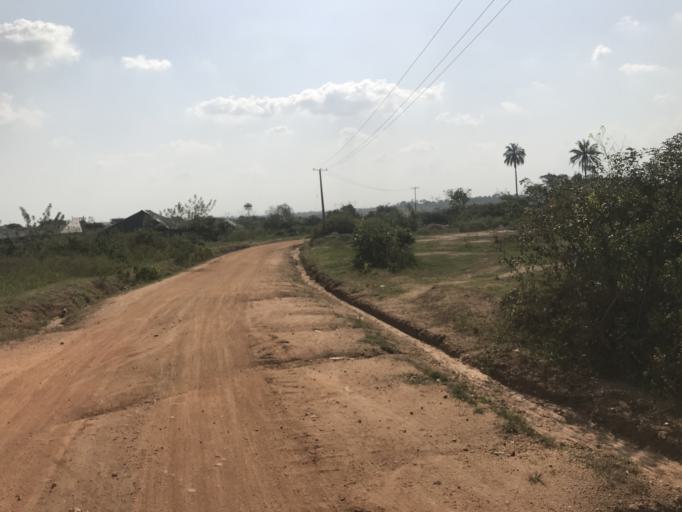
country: NG
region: Osun
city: Osogbo
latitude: 7.8448
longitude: 4.5811
